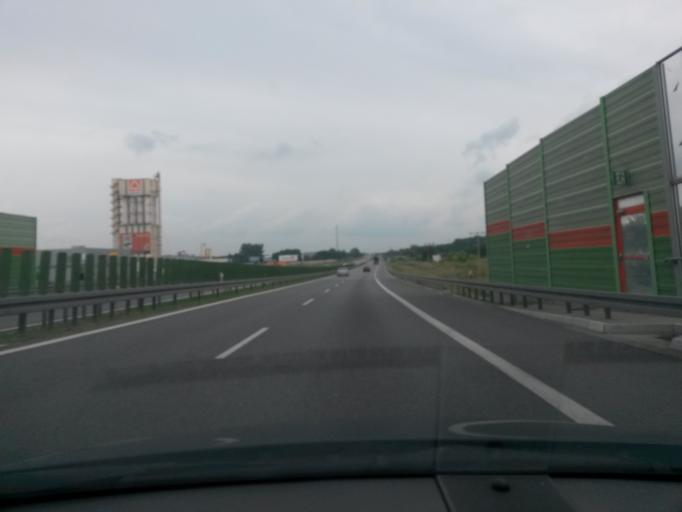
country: PL
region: Lodz Voivodeship
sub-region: Powiat rawski
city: Rawa Mazowiecka
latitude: 51.7647
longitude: 20.2690
